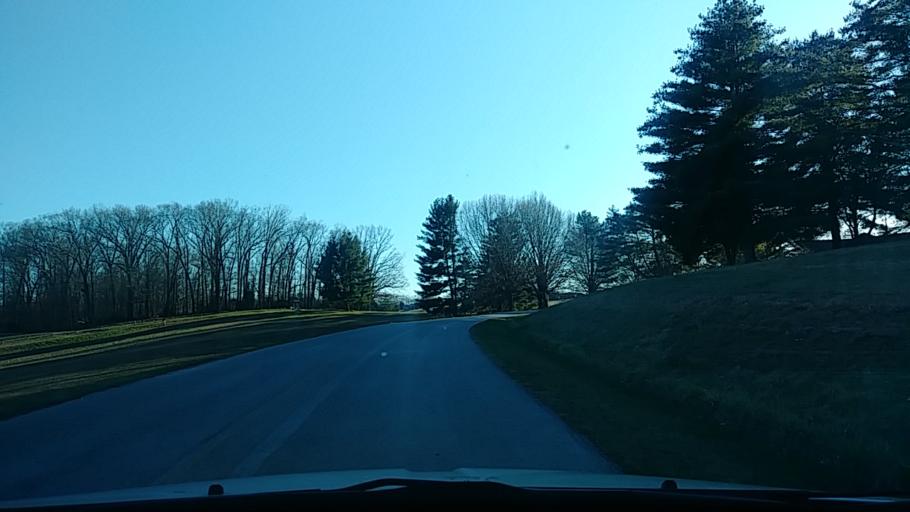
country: US
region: Tennessee
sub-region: Hamblen County
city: Morristown
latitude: 36.2078
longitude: -83.4052
